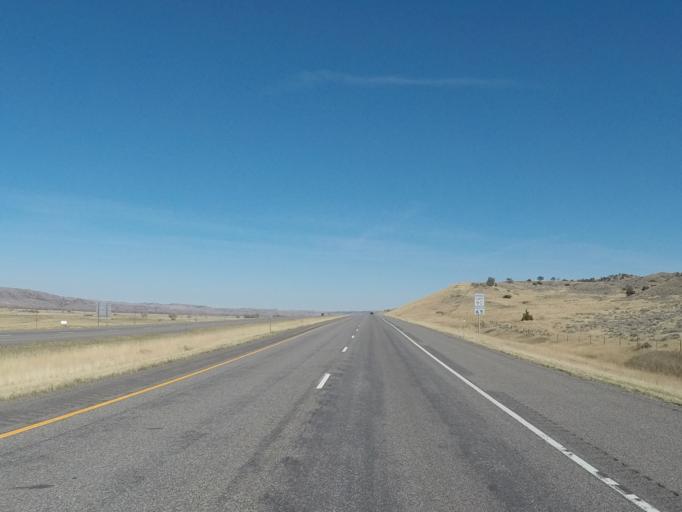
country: US
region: Montana
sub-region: Sweet Grass County
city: Big Timber
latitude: 45.7847
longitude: -110.0540
